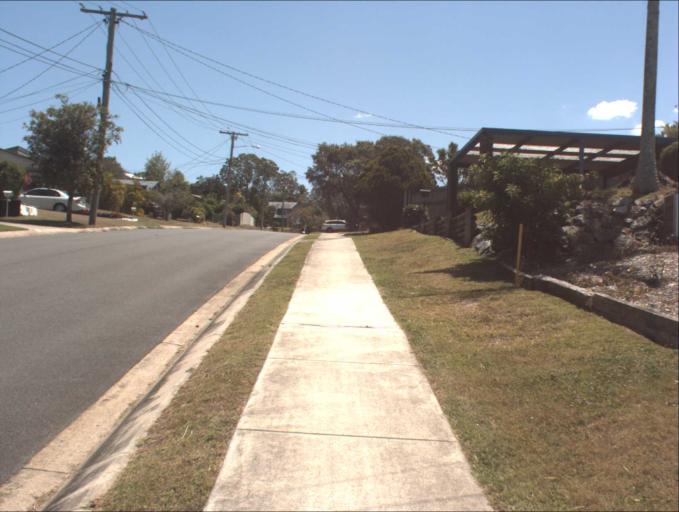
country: AU
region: Queensland
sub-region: Logan
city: Springwood
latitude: -27.6064
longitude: 153.1362
